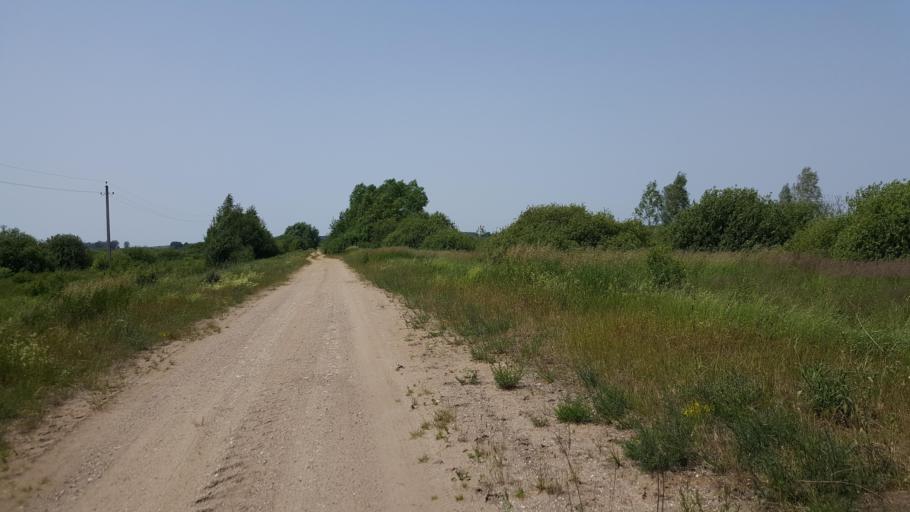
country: BY
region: Brest
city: Kamyanyets
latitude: 52.4751
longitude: 23.9108
